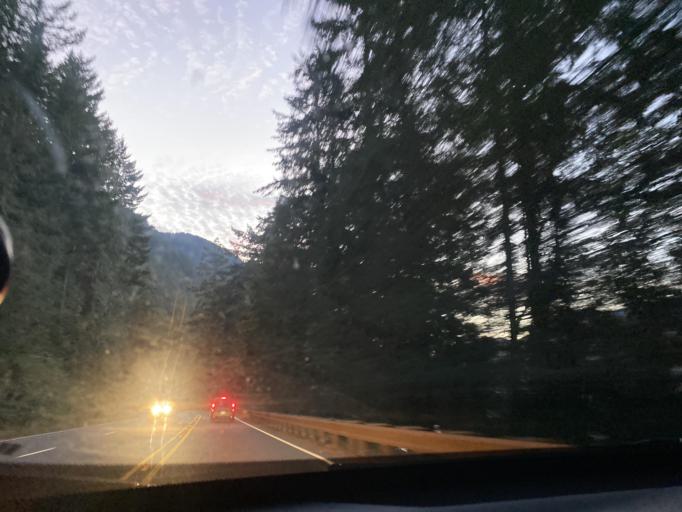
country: CA
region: British Columbia
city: Sooke
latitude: 48.0496
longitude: -123.8511
